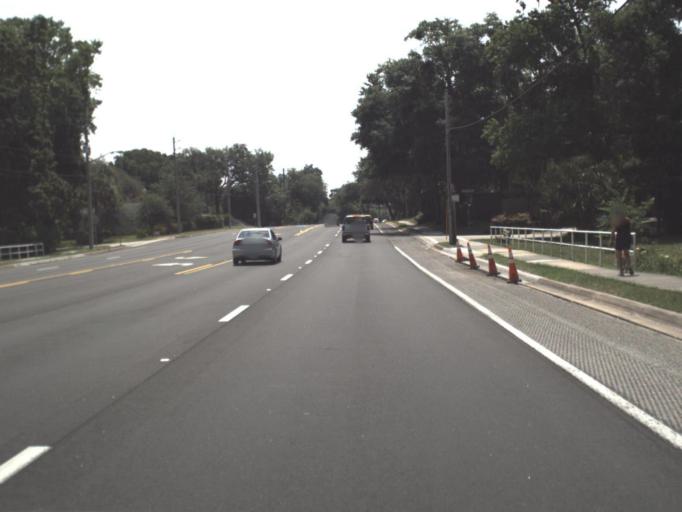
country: US
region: Florida
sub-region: Duval County
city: Jacksonville
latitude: 30.2467
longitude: -81.6320
